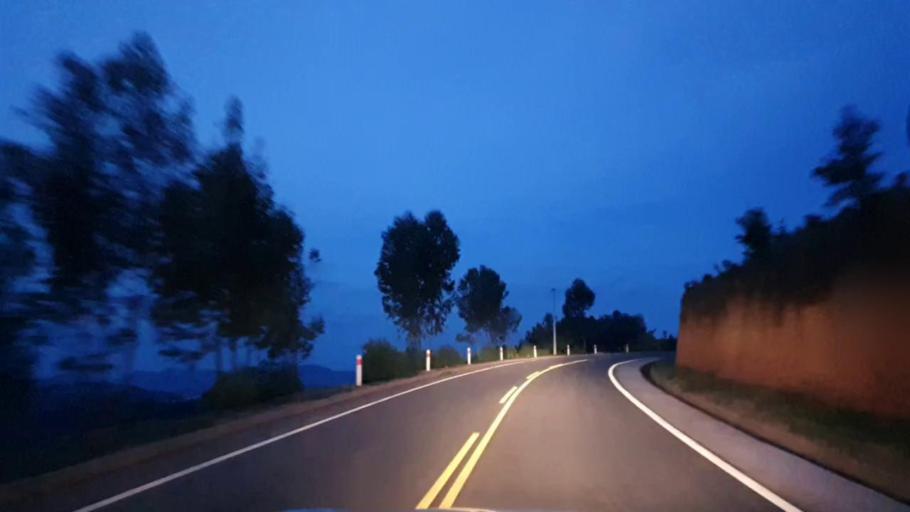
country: RW
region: Southern Province
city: Gikongoro
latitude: -2.4661
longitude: 29.5724
